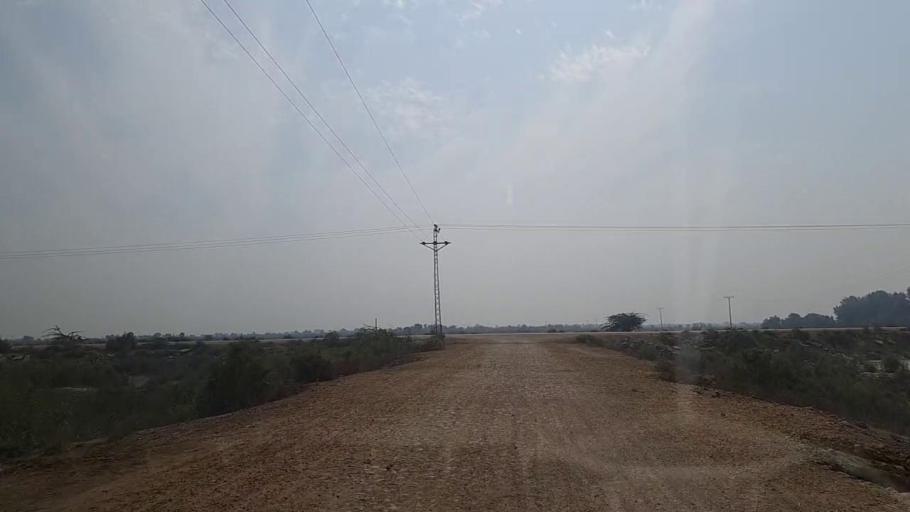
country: PK
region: Sindh
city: Mirpur Batoro
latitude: 24.5981
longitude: 68.2151
